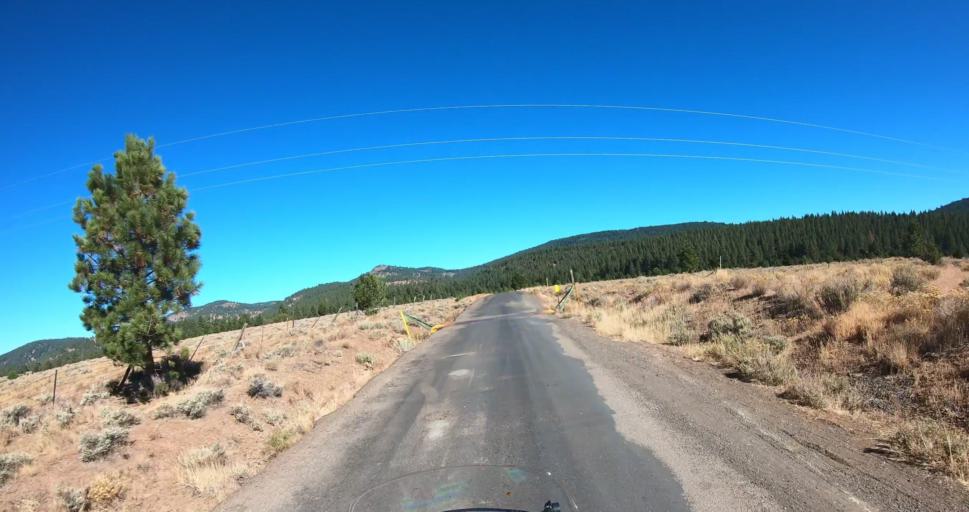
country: US
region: Oregon
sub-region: Lake County
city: Lakeview
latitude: 42.2178
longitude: -120.2285
